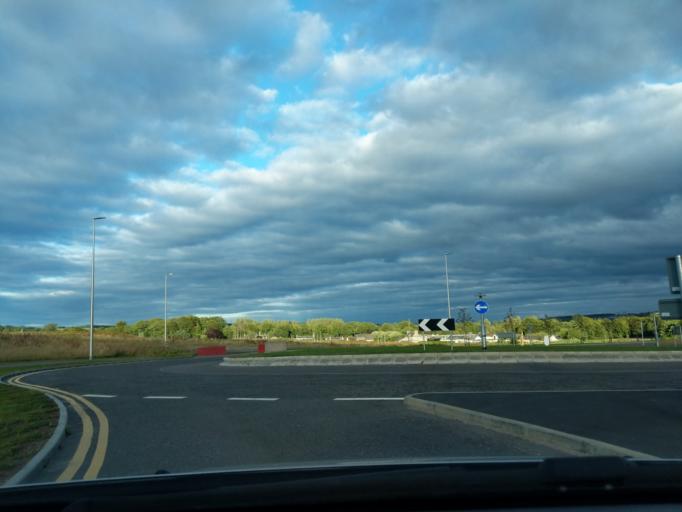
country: GB
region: Scotland
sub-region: Aberdeen City
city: Dyce
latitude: 57.1876
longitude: -2.1893
